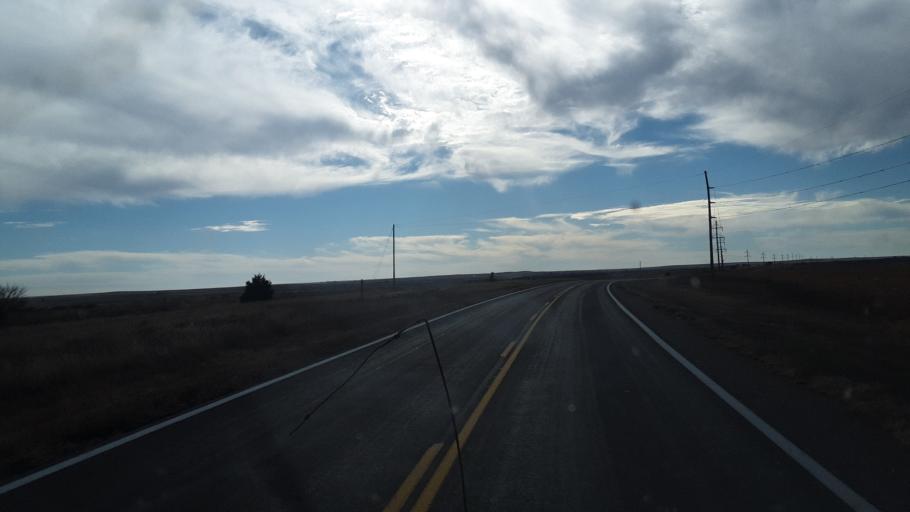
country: US
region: Kansas
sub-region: Hodgeman County
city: Jetmore
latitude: 38.1005
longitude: -99.7417
